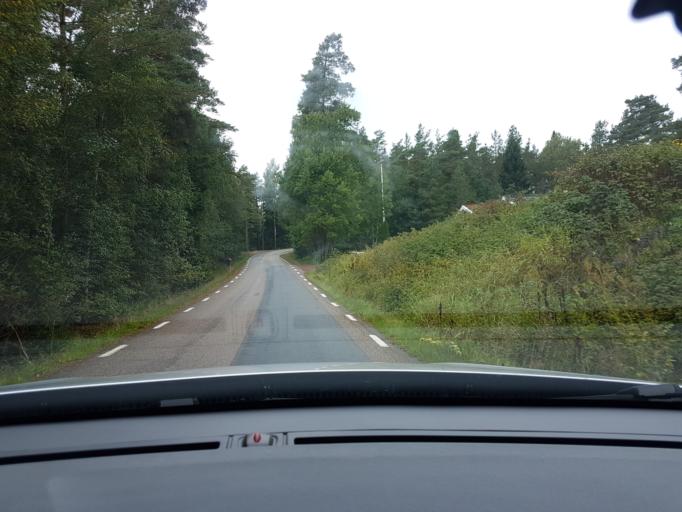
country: SE
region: Vaestra Goetaland
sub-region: Ale Kommun
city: Alvangen
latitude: 57.9052
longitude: 12.1753
